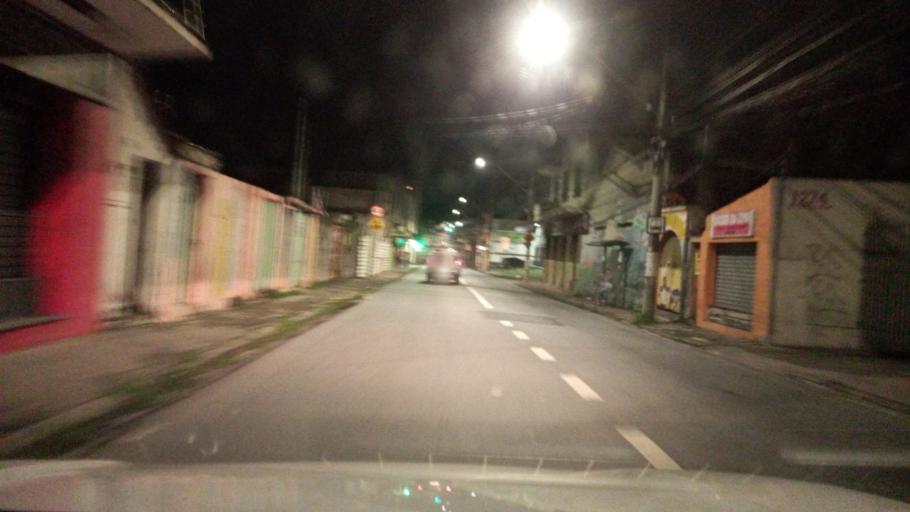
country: BR
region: Minas Gerais
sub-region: Belo Horizonte
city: Belo Horizonte
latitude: -19.9123
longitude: -43.9650
